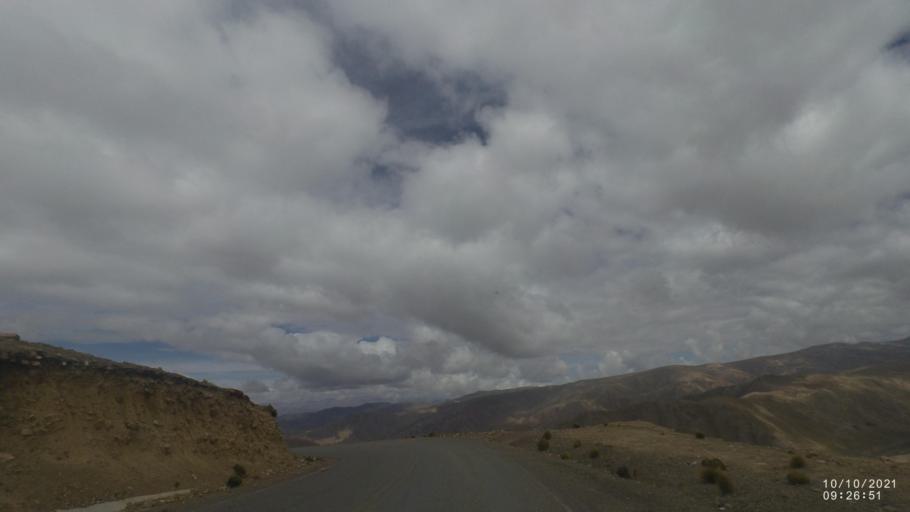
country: BO
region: La Paz
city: Quime
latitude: -17.0958
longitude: -67.3237
